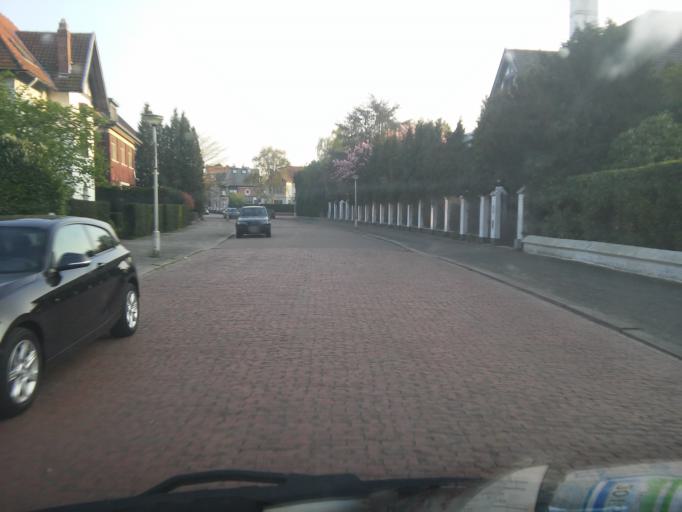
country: BE
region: Flanders
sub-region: Provincie Antwerpen
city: Antwerpen
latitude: 51.1773
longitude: 4.4030
